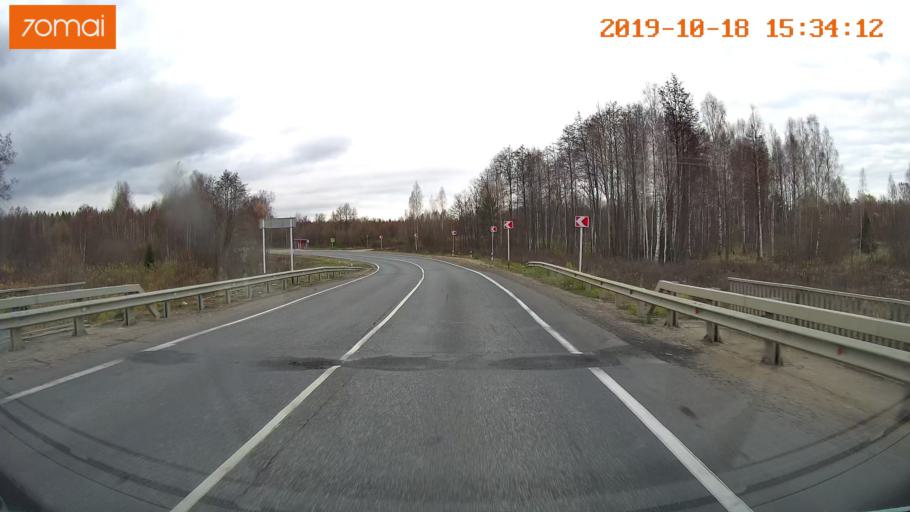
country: RU
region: Vladimir
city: Anopino
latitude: 55.8520
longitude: 40.6449
